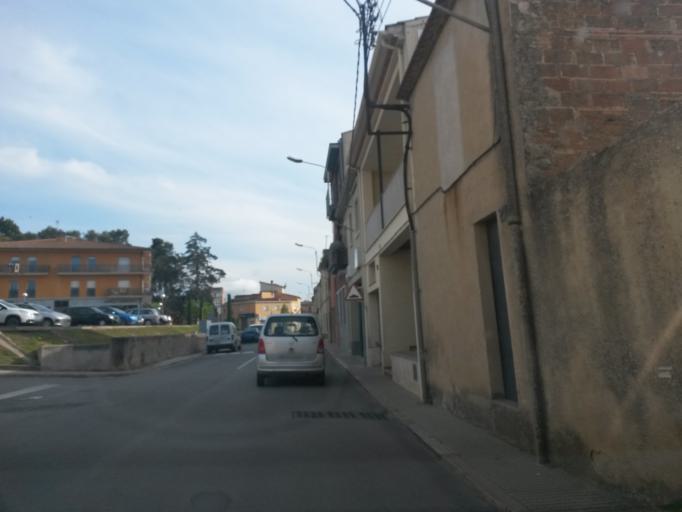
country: ES
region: Catalonia
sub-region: Provincia de Girona
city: Caldes de Malavella
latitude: 41.8403
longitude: 2.8097
